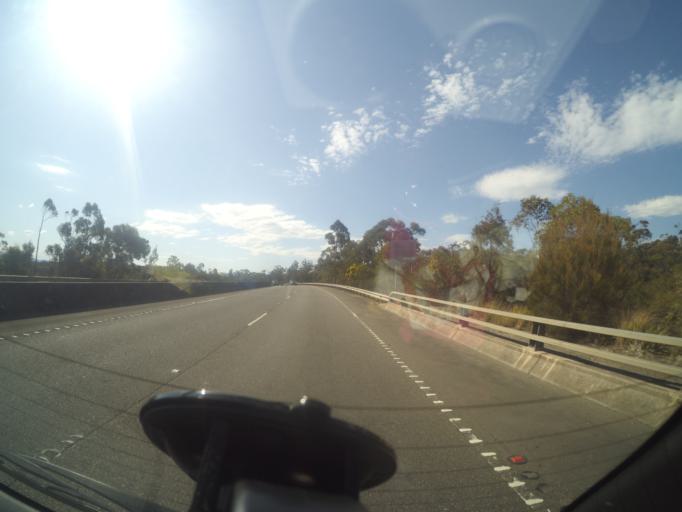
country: AU
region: New South Wales
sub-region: Blue Mountains Municipality
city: Hazelbrook
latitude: -33.7241
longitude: 150.4934
